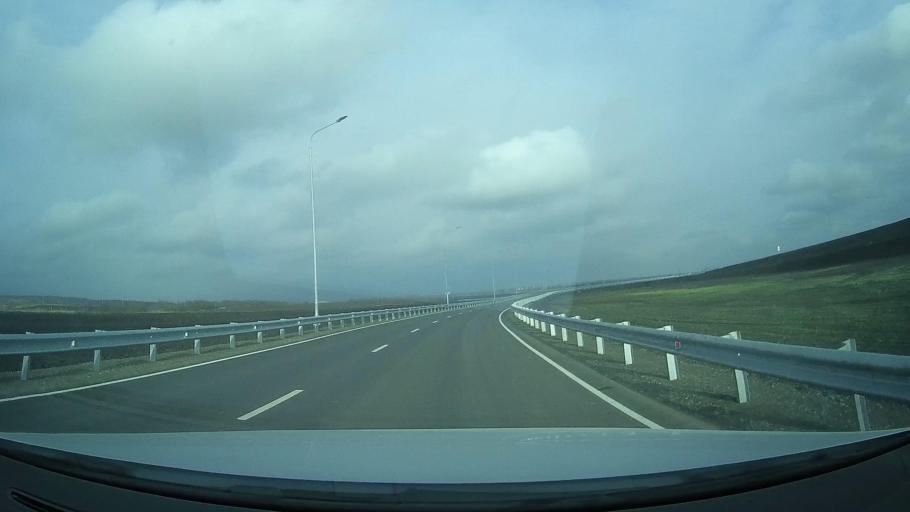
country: RU
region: Rostov
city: Grushevskaya
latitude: 47.4569
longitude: 39.8837
